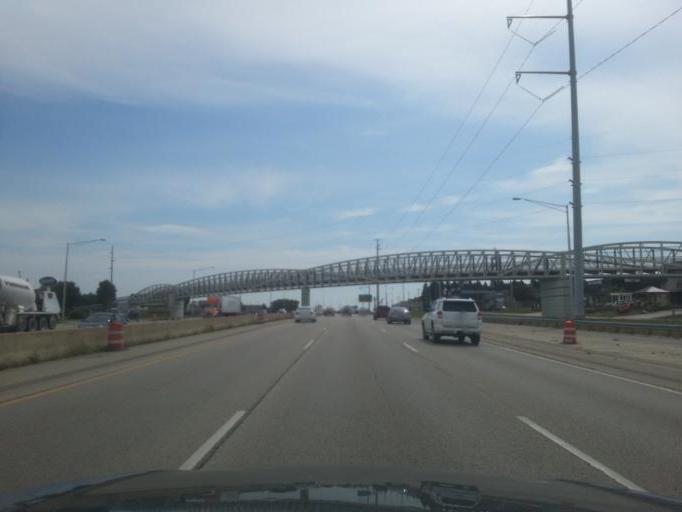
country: US
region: Wisconsin
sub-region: Dane County
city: Madison
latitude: 43.0350
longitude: -89.4171
